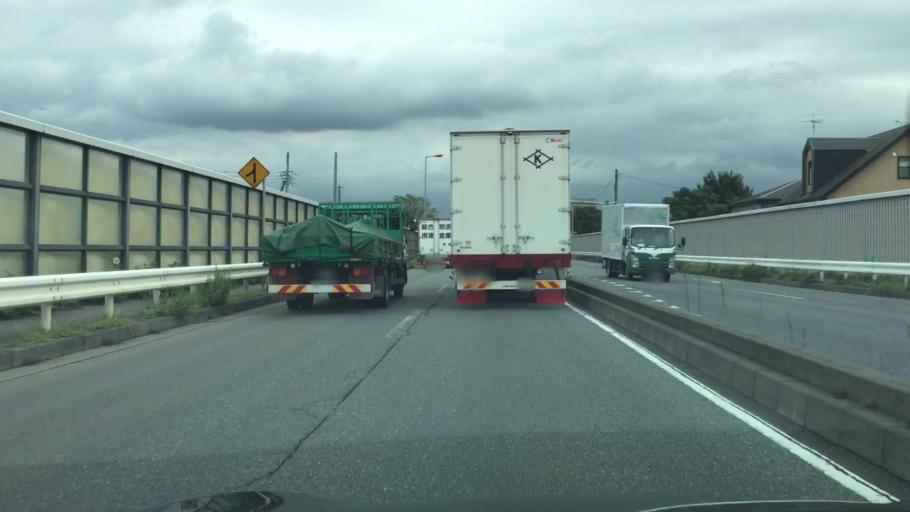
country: JP
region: Saitama
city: Kamifukuoka
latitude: 35.9138
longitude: 139.5319
